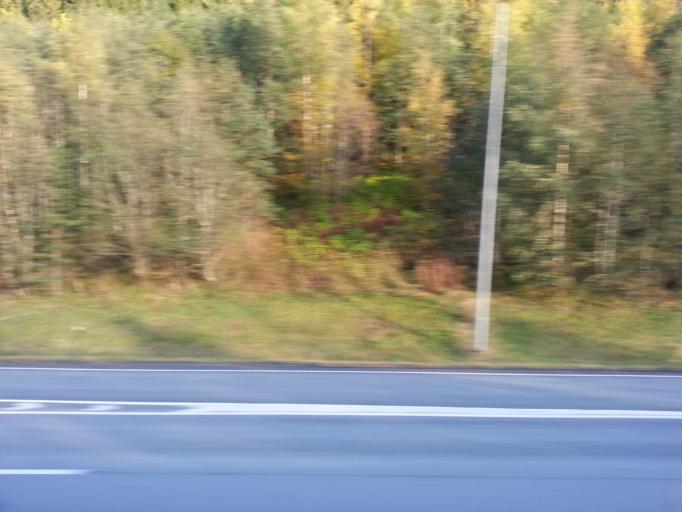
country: NO
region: Sor-Trondelag
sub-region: Malvik
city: Hommelvik
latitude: 63.4105
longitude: 10.8163
